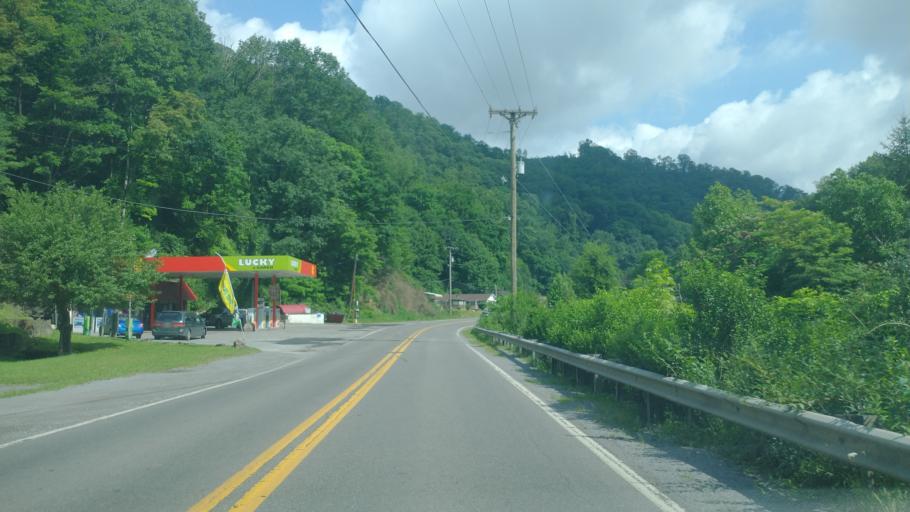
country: US
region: West Virginia
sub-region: McDowell County
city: Welch
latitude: 37.3938
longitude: -81.4219
